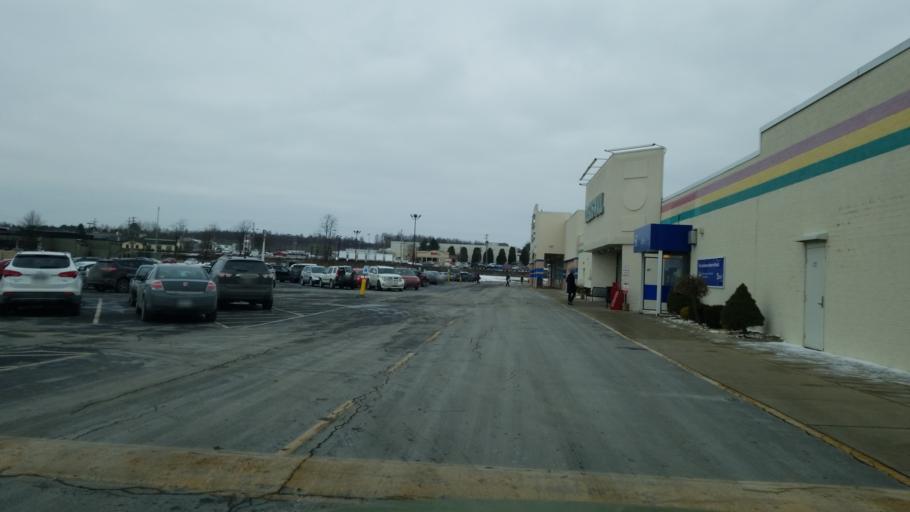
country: US
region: Pennsylvania
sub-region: Clearfield County
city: DuBois
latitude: 41.1202
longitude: -78.7282
